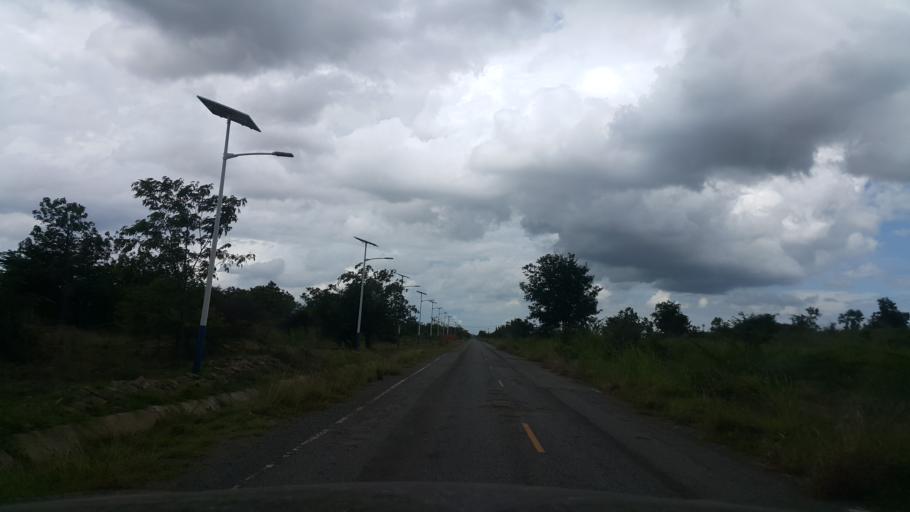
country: TH
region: Sukhothai
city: Sukhothai
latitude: 17.0613
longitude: 99.7832
